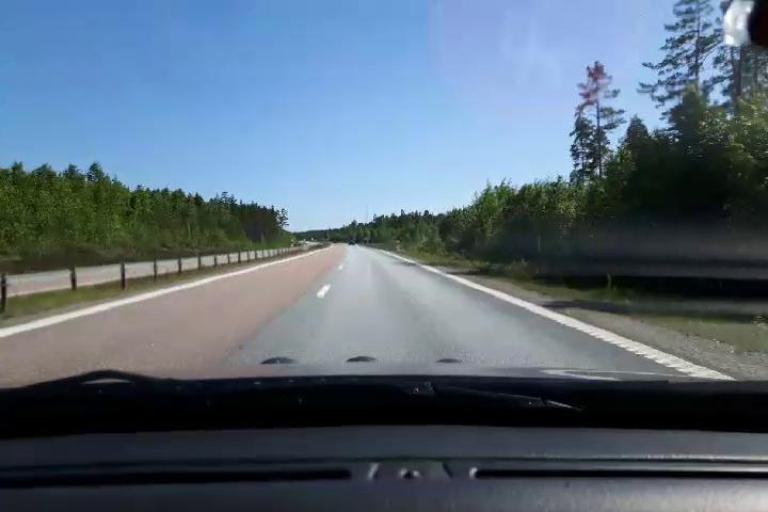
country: SE
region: Gaevleborg
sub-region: Soderhamns Kommun
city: Soderhamn
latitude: 61.4182
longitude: 16.9869
